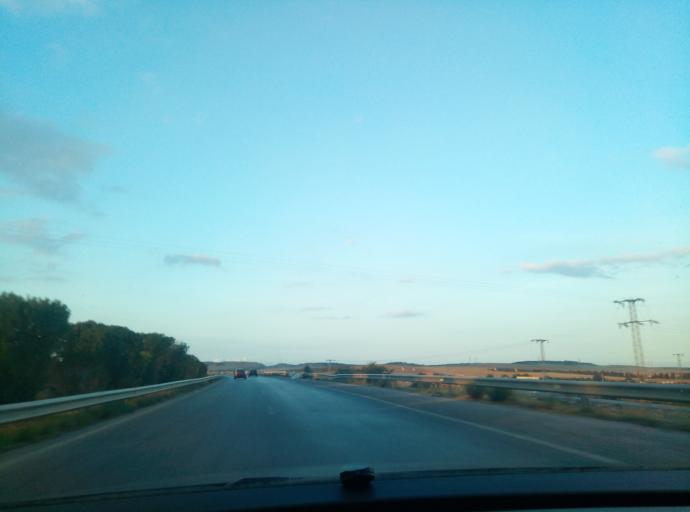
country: TN
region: Tunis
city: Oued Lill
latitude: 36.7393
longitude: 10.0295
